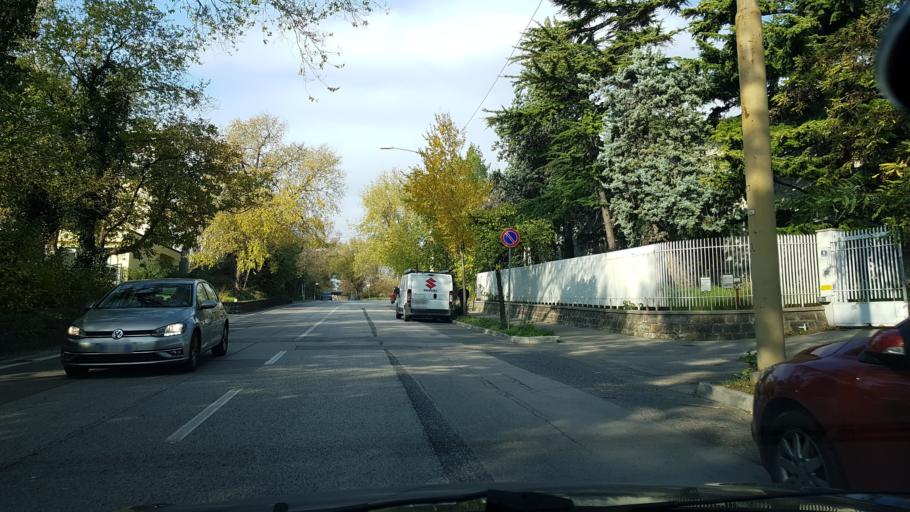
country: IT
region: Friuli Venezia Giulia
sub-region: Provincia di Trieste
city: Trieste
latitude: 45.6193
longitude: 13.8013
